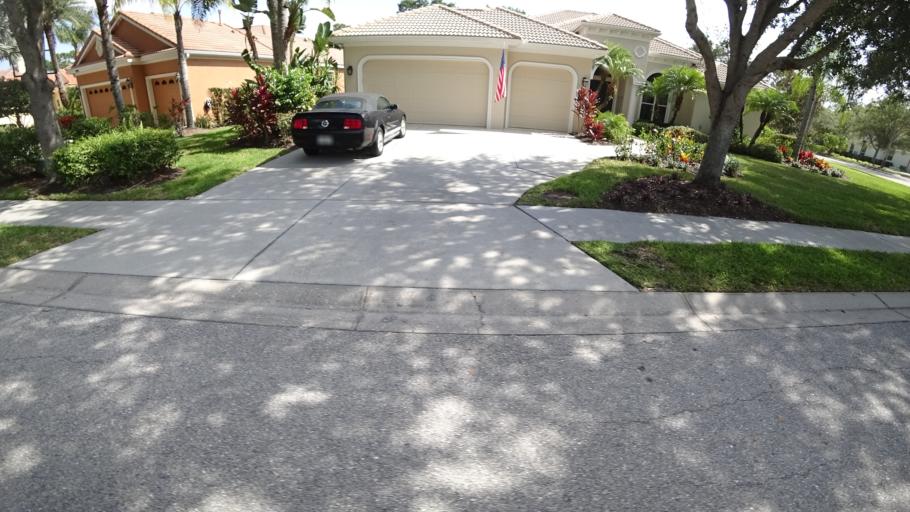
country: US
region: Florida
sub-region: Sarasota County
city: The Meadows
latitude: 27.4044
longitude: -82.4428
